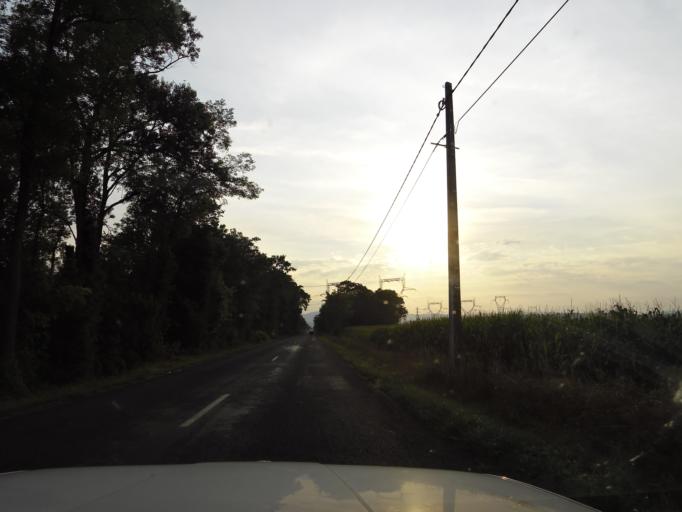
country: FR
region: Rhone-Alpes
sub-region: Departement de l'Ain
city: Saint-Jean-de-Niost
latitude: 45.8149
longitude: 5.2235
